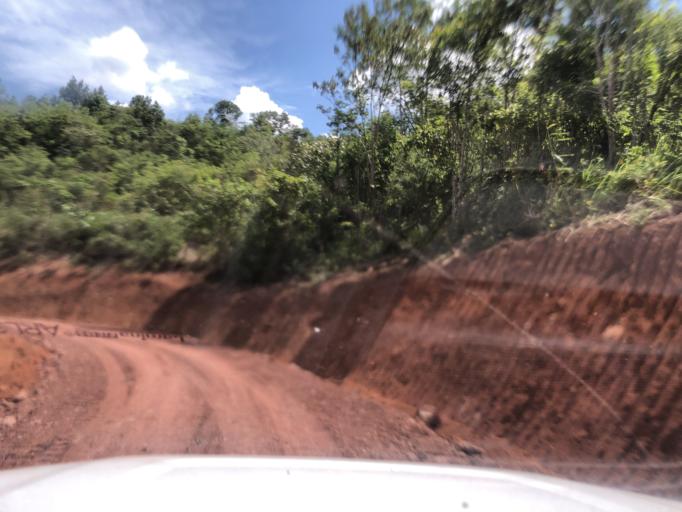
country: CN
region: Yunnan
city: Menglie
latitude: 22.2335
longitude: 101.6197
